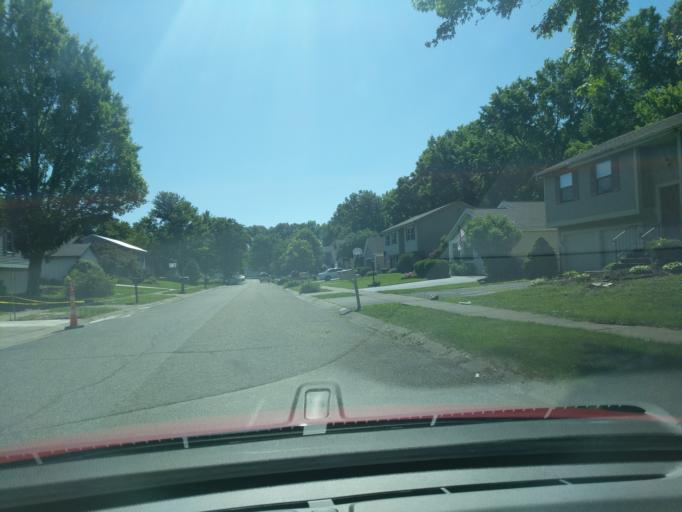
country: US
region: Ohio
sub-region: Franklin County
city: Huber Ridge
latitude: 40.0642
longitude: -82.9110
